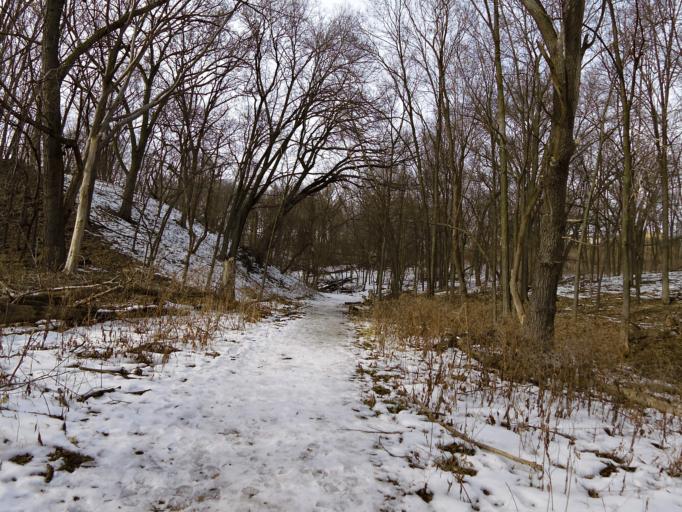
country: US
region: Minnesota
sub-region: Hennepin County
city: Richfield
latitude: 44.8578
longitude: -93.2155
